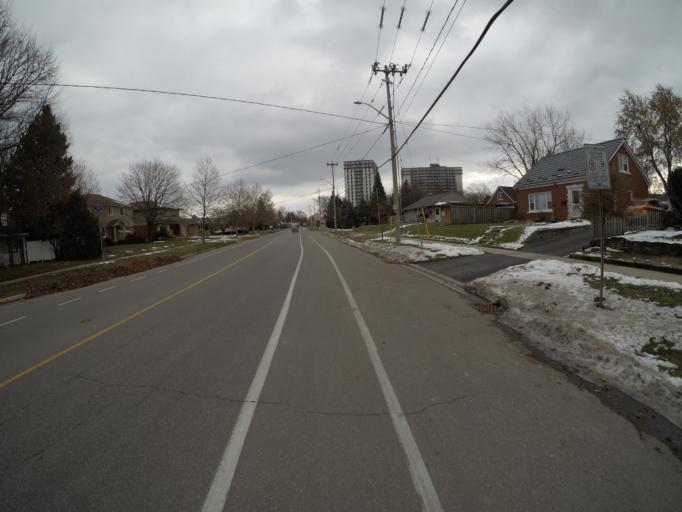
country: CA
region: Ontario
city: Waterloo
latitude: 43.4661
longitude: -80.4984
